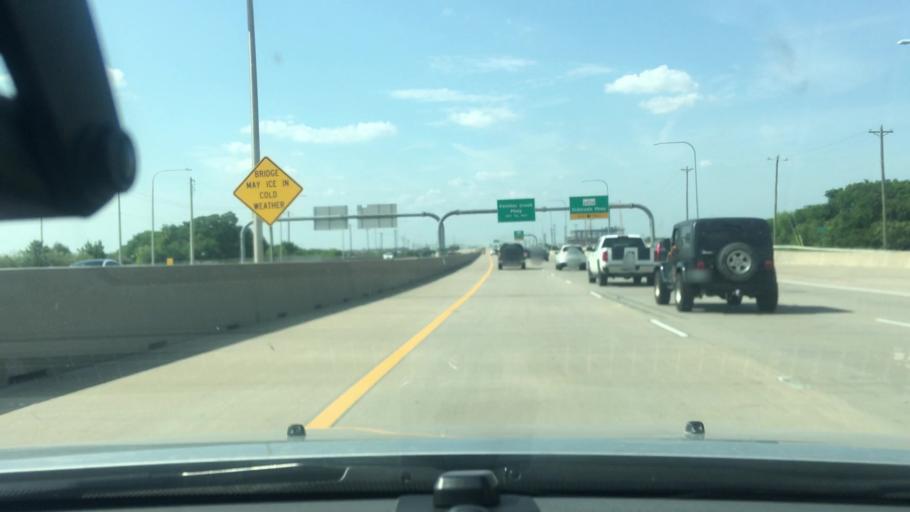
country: US
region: Texas
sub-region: Collin County
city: Frisco
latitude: 33.1656
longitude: -96.8399
